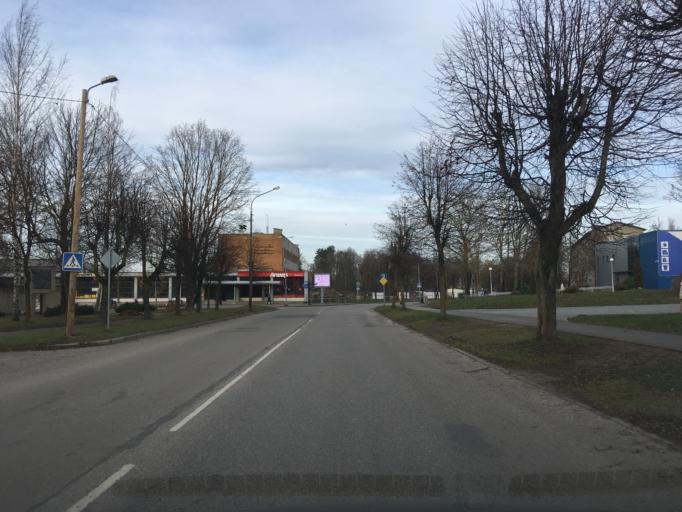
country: EE
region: Ida-Virumaa
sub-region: Sillamaee linn
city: Sillamae
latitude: 59.3920
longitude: 27.7744
